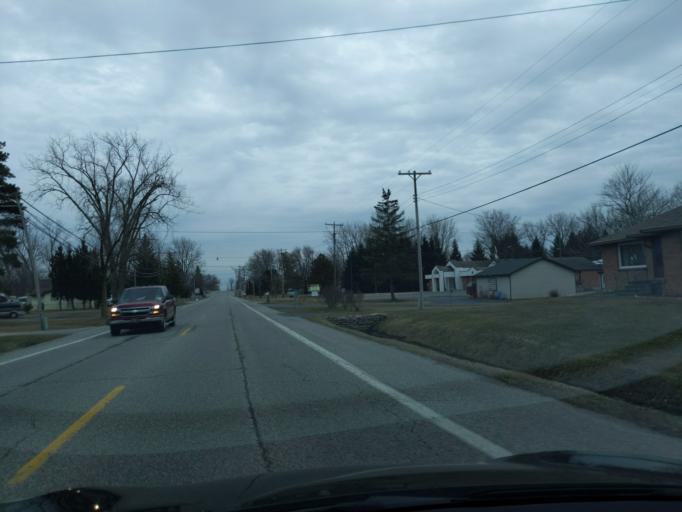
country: US
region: Michigan
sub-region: Bay County
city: Bay City
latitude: 43.6414
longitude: -83.9135
